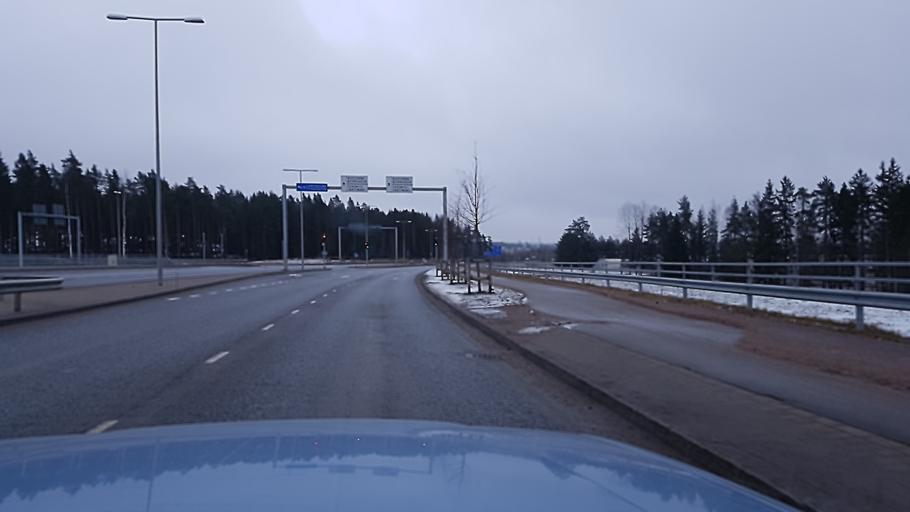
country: FI
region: Uusimaa
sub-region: Helsinki
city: Vantaa
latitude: 60.3015
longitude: 24.9616
